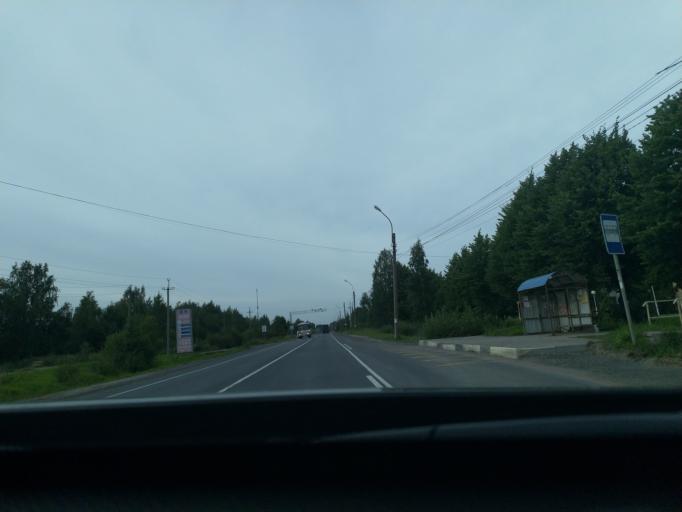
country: RU
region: Leningrad
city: Nikol'skoye
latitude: 59.7230
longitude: 30.7783
